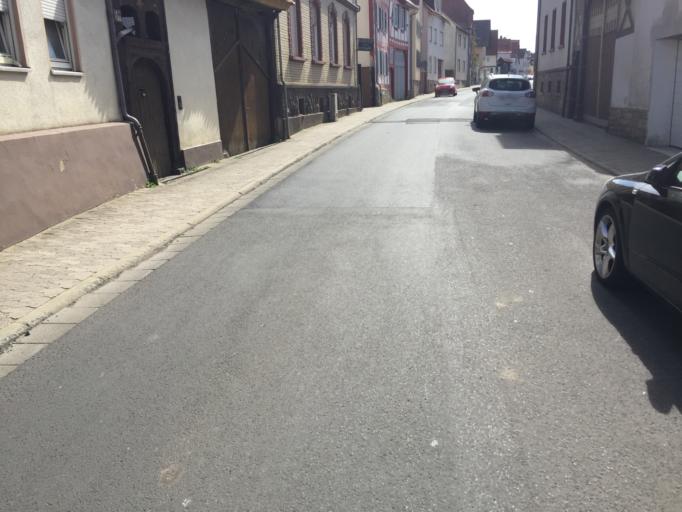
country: DE
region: Hesse
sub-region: Regierungsbezirk Giessen
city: Langgons
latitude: 50.4716
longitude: 8.6537
